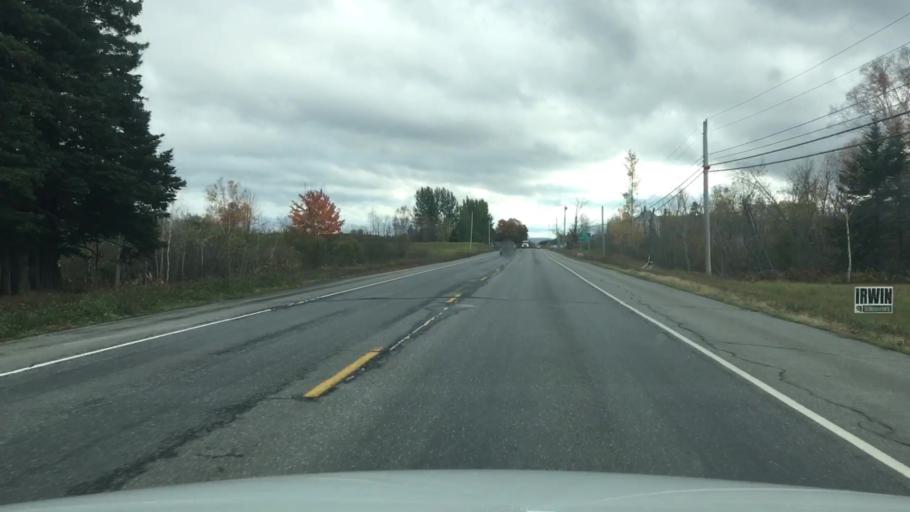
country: US
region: Maine
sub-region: Aroostook County
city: Houlton
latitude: 46.1849
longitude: -67.8412
